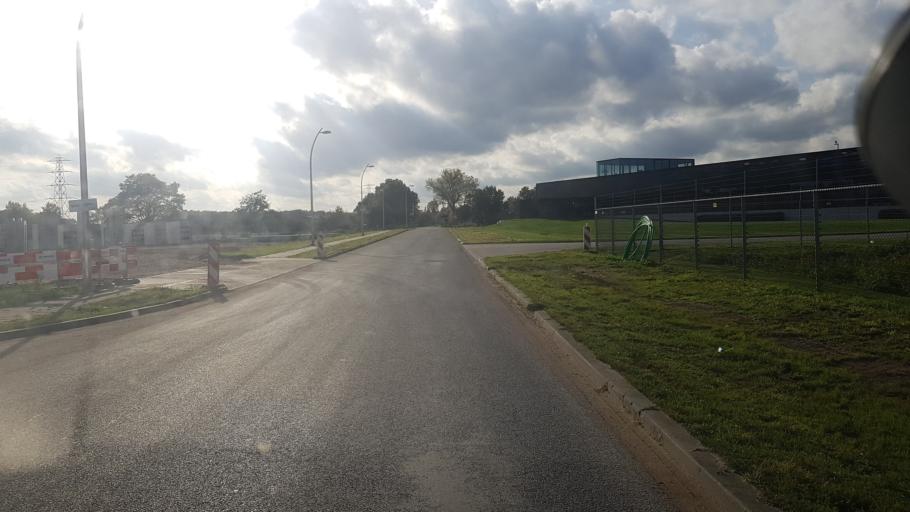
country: NL
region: Gelderland
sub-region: Gemeente Apeldoorn
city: Apeldoorn
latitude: 52.1960
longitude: 6.0327
